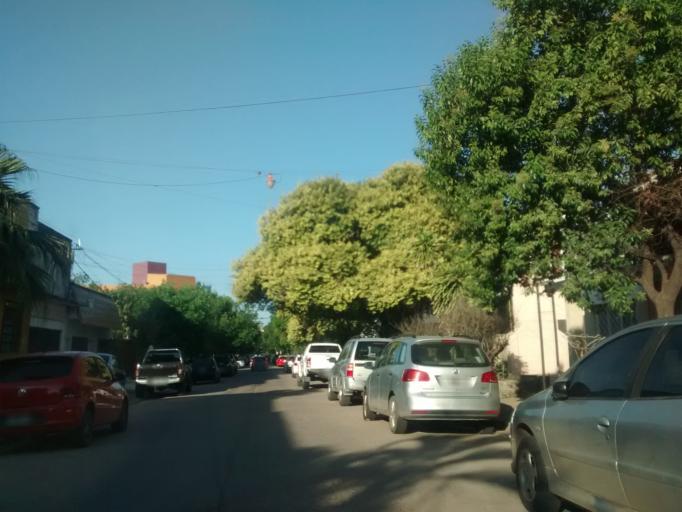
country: AR
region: Chaco
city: Resistencia
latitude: -27.4571
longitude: -58.9827
